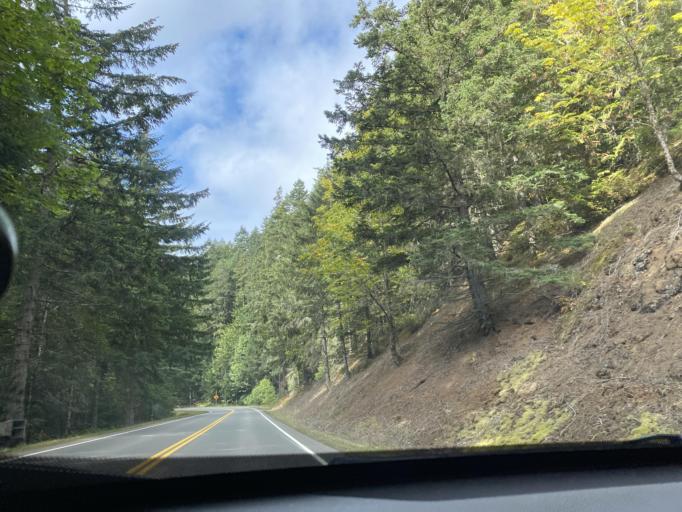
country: US
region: Washington
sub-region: Clallam County
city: Port Angeles
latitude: 48.0428
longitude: -123.4208
